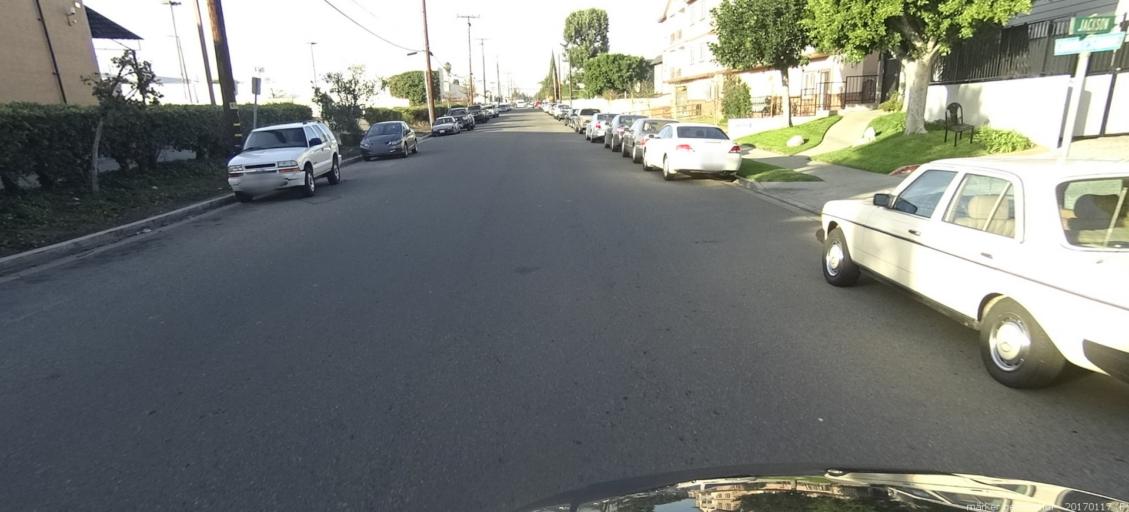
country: US
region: California
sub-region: Orange County
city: Midway City
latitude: 33.7388
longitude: -117.9874
